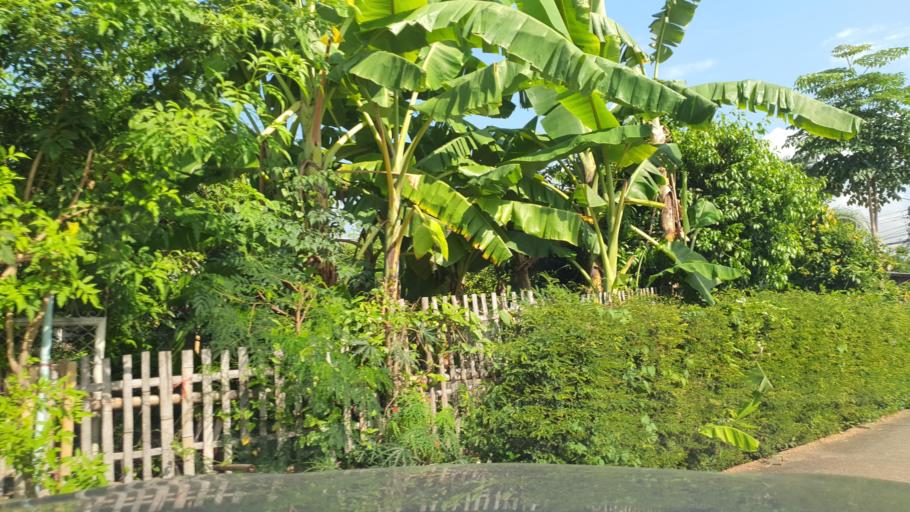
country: TH
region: Chiang Mai
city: Hang Dong
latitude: 18.7119
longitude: 98.9195
